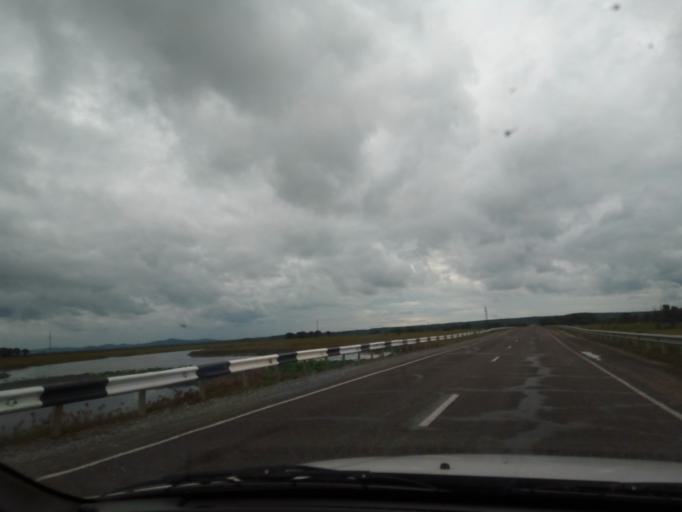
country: RU
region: Primorskiy
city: Dal'nerechensk
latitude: 45.9127
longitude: 133.7662
